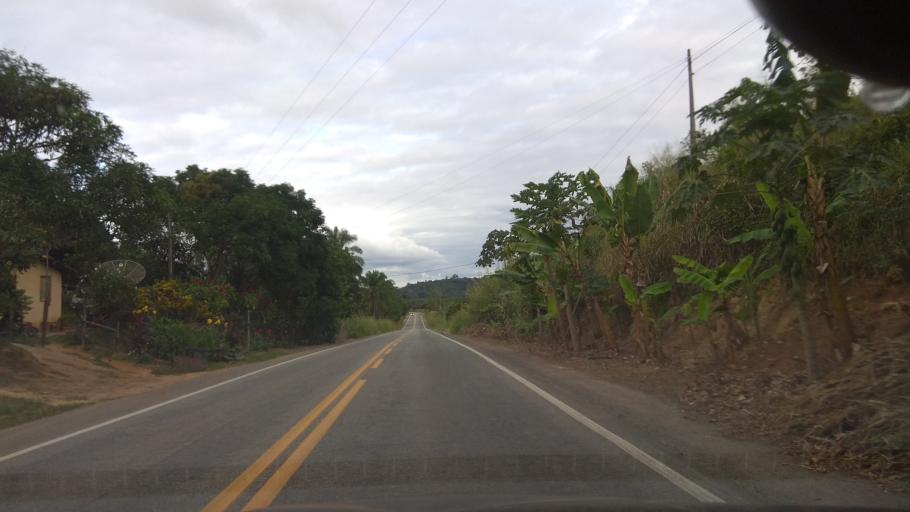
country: BR
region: Bahia
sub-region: Ipiau
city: Ipiau
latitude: -14.1685
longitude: -39.6855
